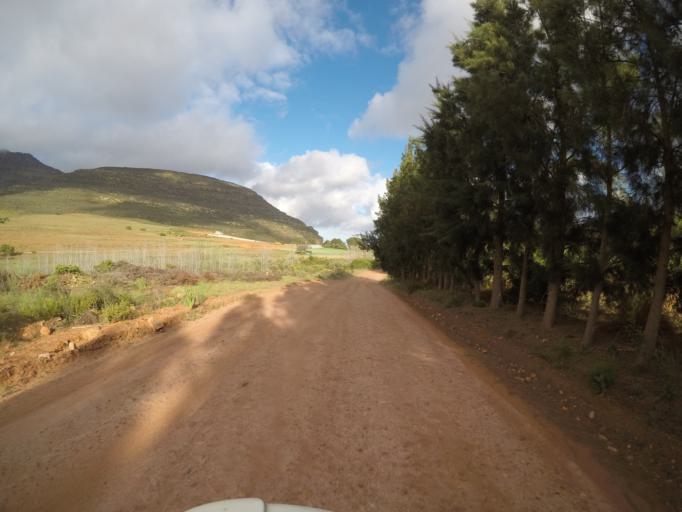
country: ZA
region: Western Cape
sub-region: West Coast District Municipality
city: Clanwilliam
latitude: -32.3404
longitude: 18.8003
